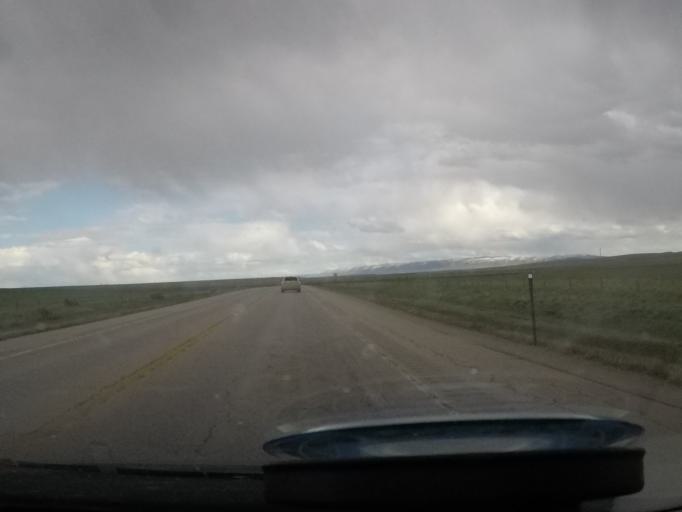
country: US
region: Wyoming
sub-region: Natrona County
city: Mills
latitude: 42.9557
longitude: -106.6476
